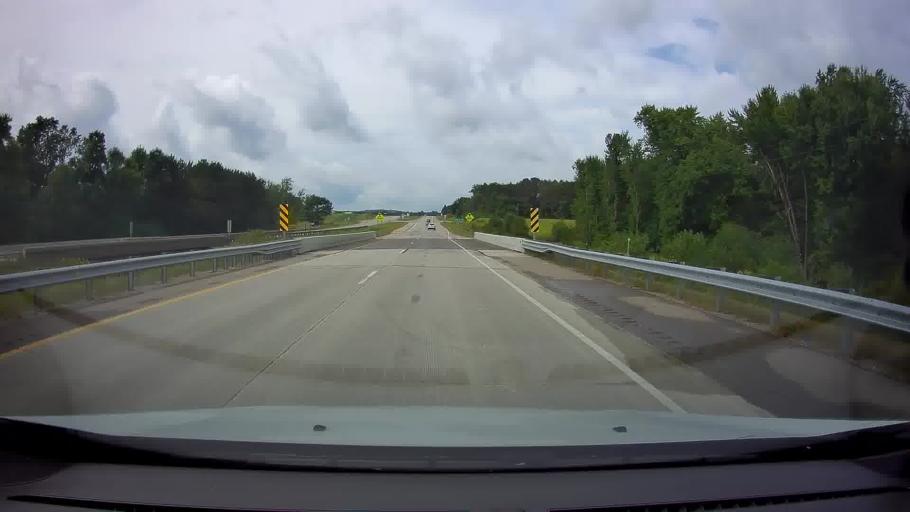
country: US
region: Wisconsin
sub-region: Shawano County
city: Wittenberg
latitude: 44.8039
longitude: -89.0160
